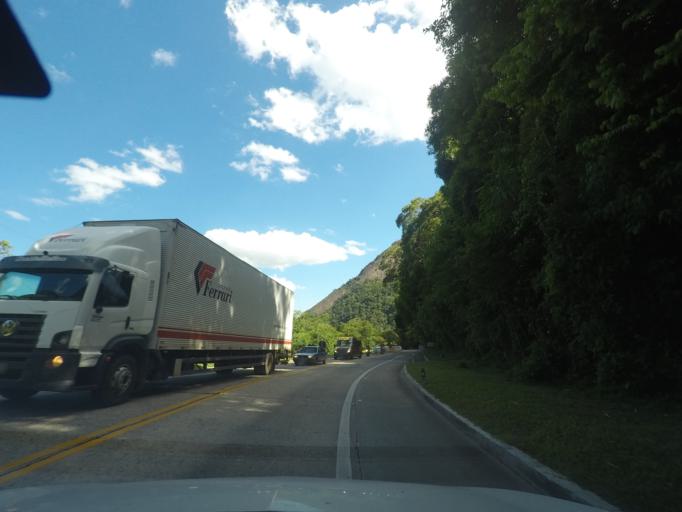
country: BR
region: Rio de Janeiro
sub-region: Teresopolis
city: Teresopolis
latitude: -22.4689
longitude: -43.0014
